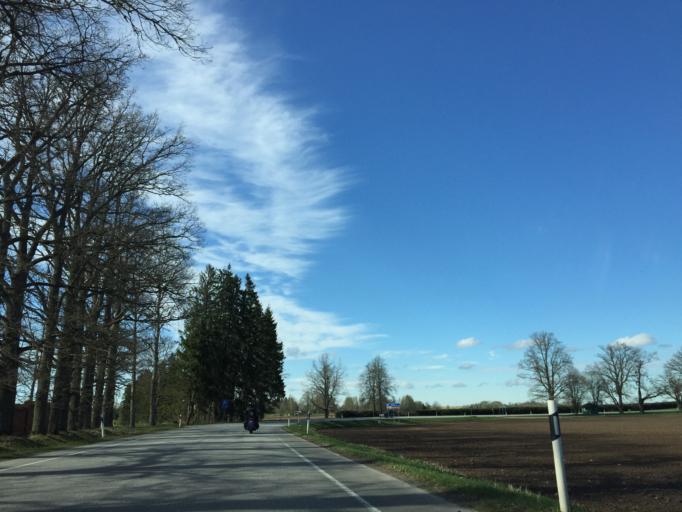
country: EE
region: Vorumaa
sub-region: Antsla vald
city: Vana-Antsla
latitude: 57.9029
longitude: 26.2862
